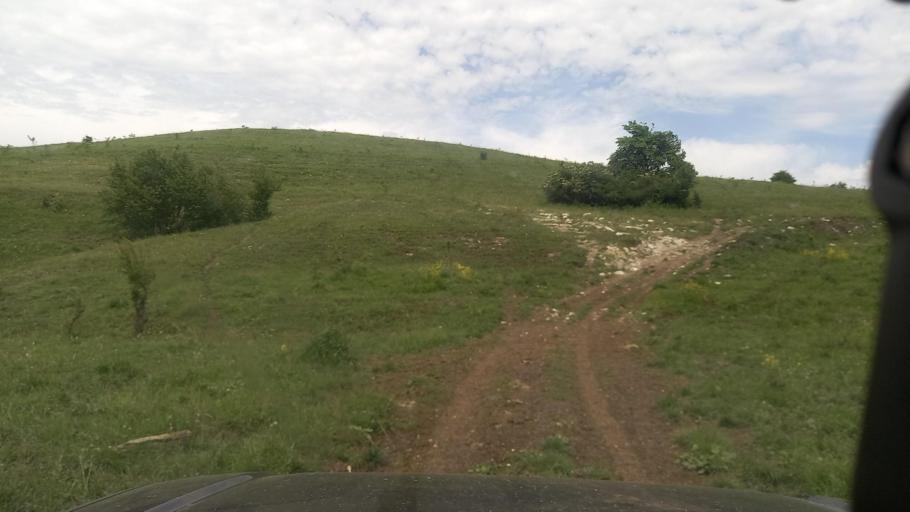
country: RU
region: Karachayevo-Cherkesiya
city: Pregradnaya
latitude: 44.0829
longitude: 41.2413
